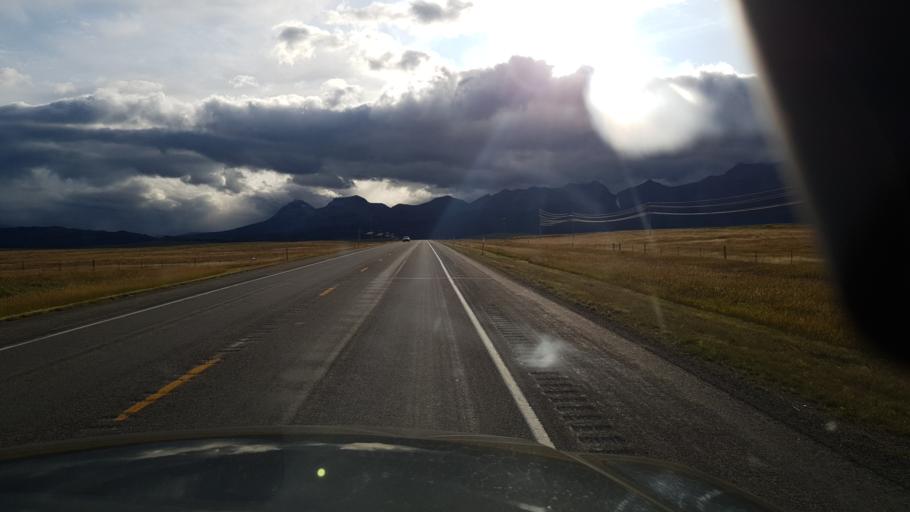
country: US
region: Montana
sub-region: Glacier County
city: South Browning
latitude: 48.4628
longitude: -113.1662
